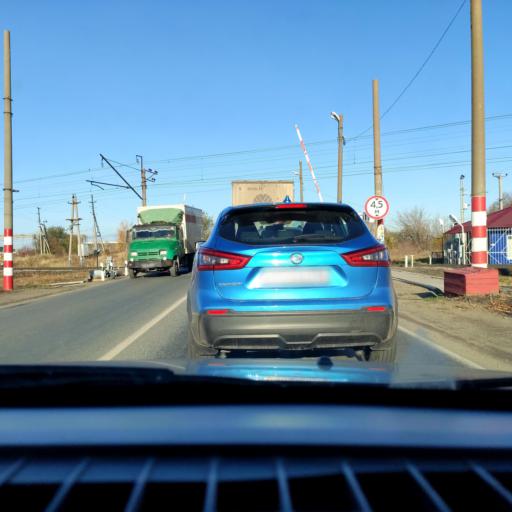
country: RU
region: Samara
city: Tol'yatti
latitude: 53.5614
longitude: 49.3568
